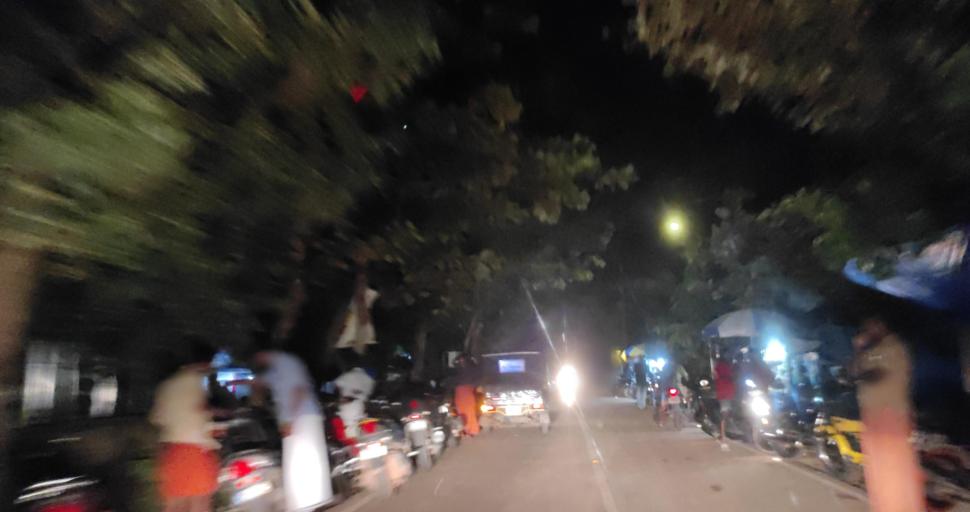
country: IN
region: Kerala
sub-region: Alappuzha
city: Vayalar
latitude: 9.7452
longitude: 76.2988
